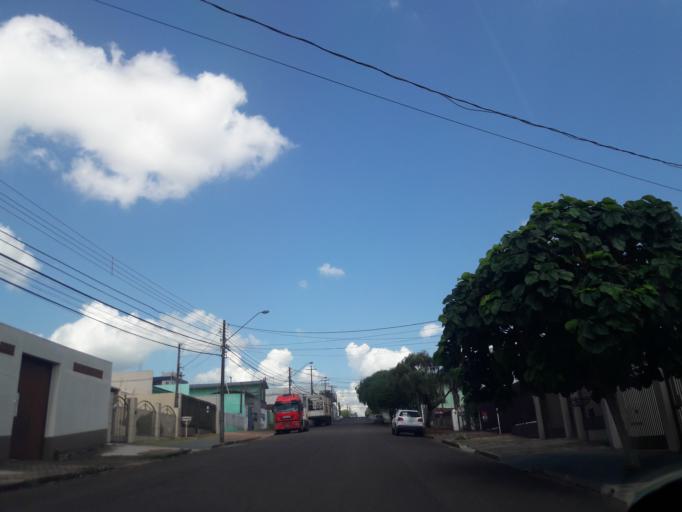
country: BR
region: Parana
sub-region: Cascavel
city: Cascavel
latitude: -24.9724
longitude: -53.4574
